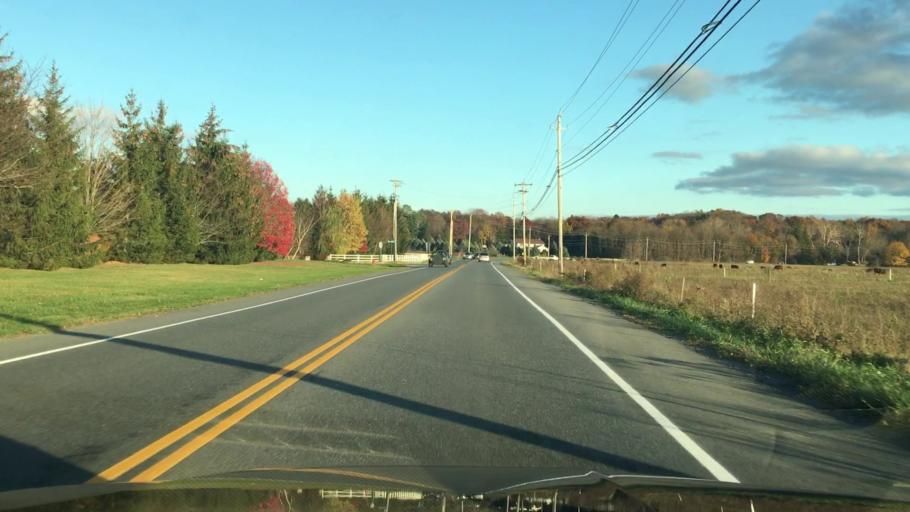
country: US
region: New York
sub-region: Dutchess County
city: Hillside Lake
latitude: 41.6448
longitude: -73.7999
